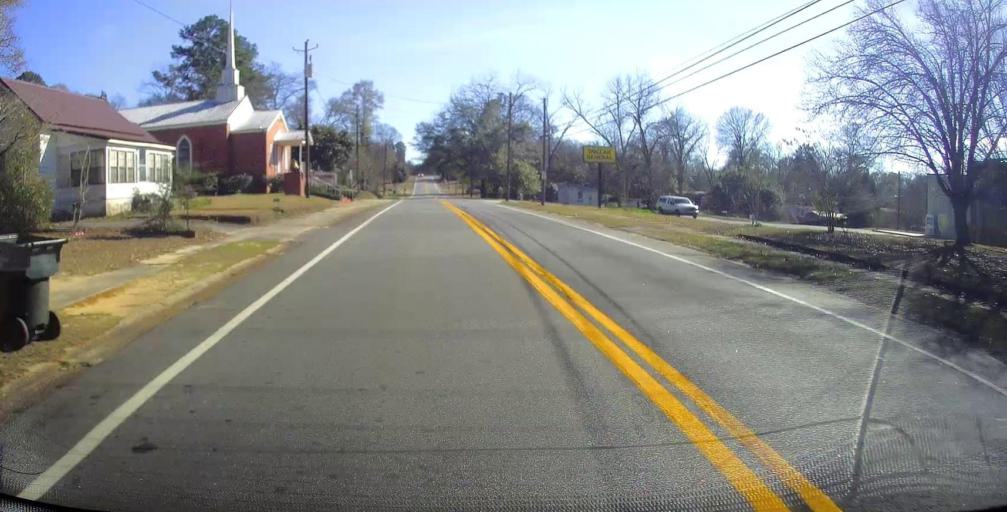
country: US
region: Georgia
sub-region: Macon County
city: Oglethorpe
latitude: 32.3741
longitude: -84.1883
